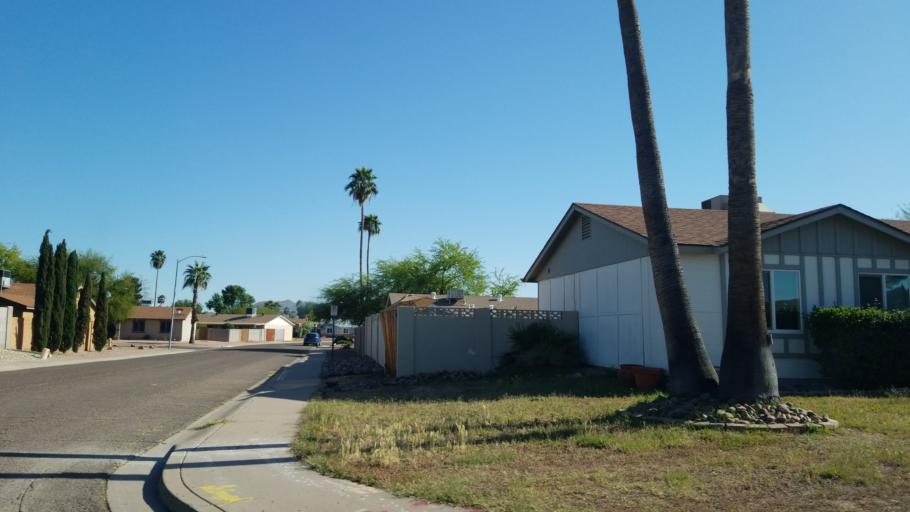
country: US
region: Arizona
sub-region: Maricopa County
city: Paradise Valley
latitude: 33.6227
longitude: -111.9985
